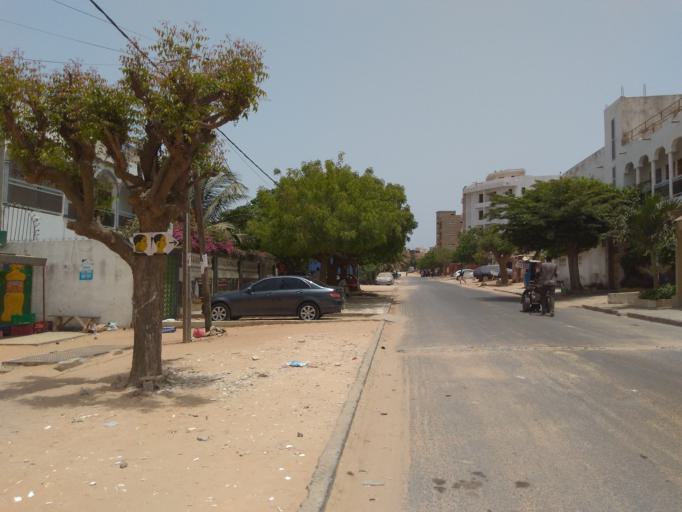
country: SN
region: Dakar
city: Grand Dakar
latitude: 14.7274
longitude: -17.4630
